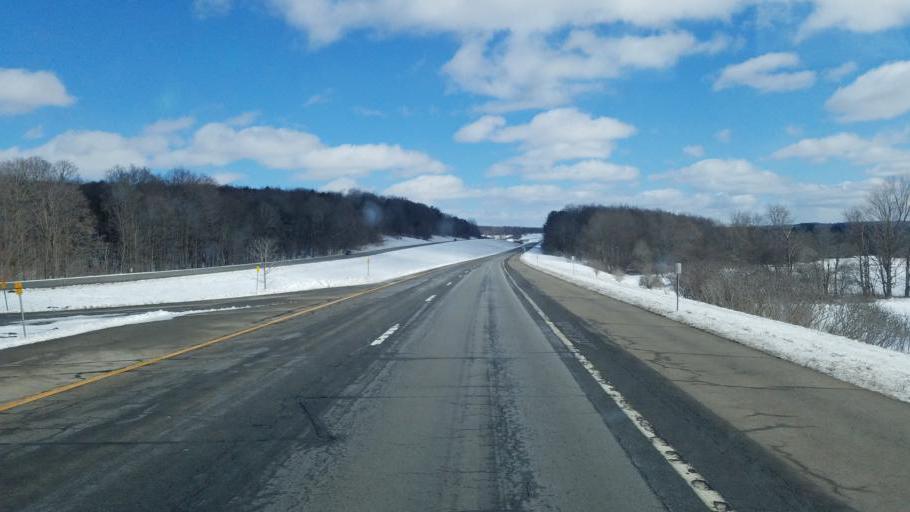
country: US
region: New York
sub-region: Chautauqua County
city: Celoron
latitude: 42.1279
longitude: -79.2930
